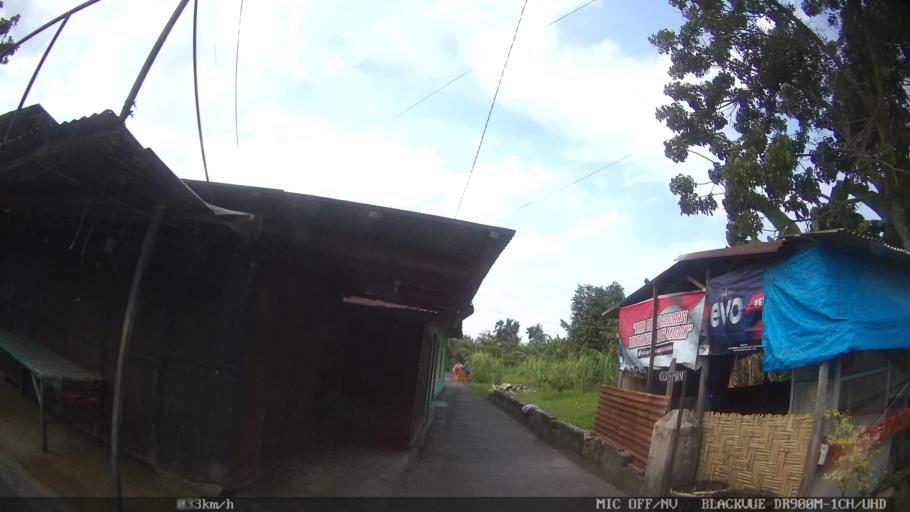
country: ID
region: North Sumatra
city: Binjai
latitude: 3.6132
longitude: 98.5166
